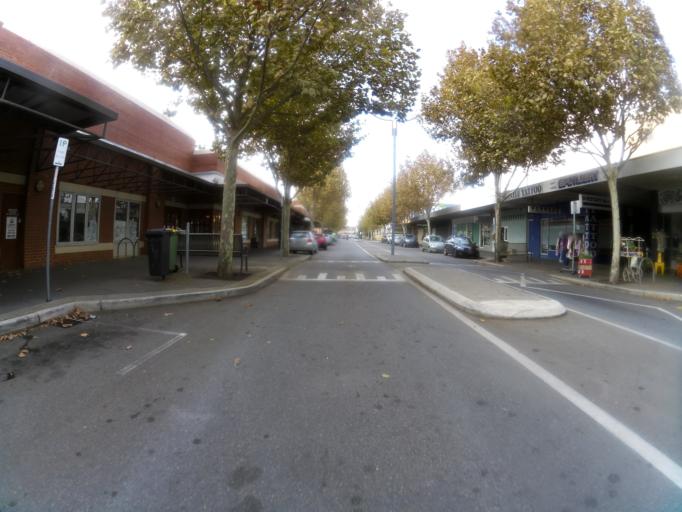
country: AU
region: Western Australia
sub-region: Fremantle
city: South Fremantle
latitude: -32.0521
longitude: 115.7475
